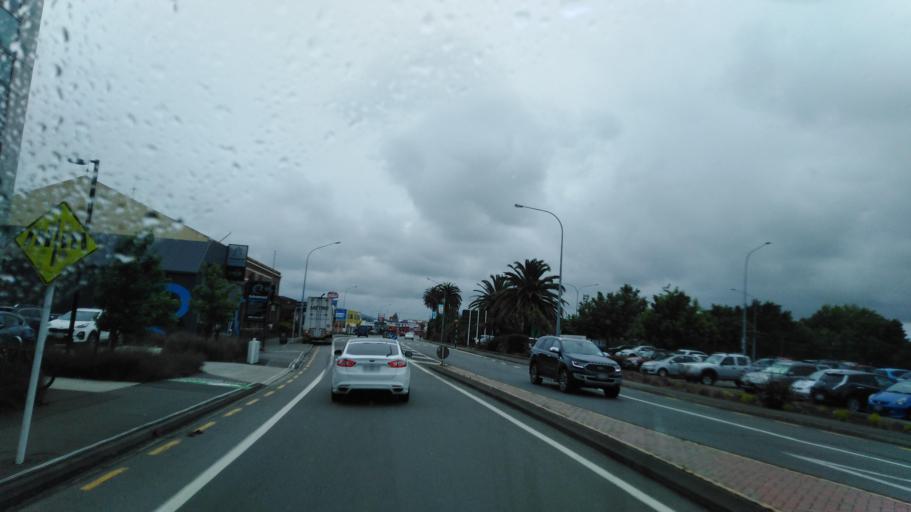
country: NZ
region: Marlborough
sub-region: Marlborough District
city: Blenheim
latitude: -41.5107
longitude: 173.9594
